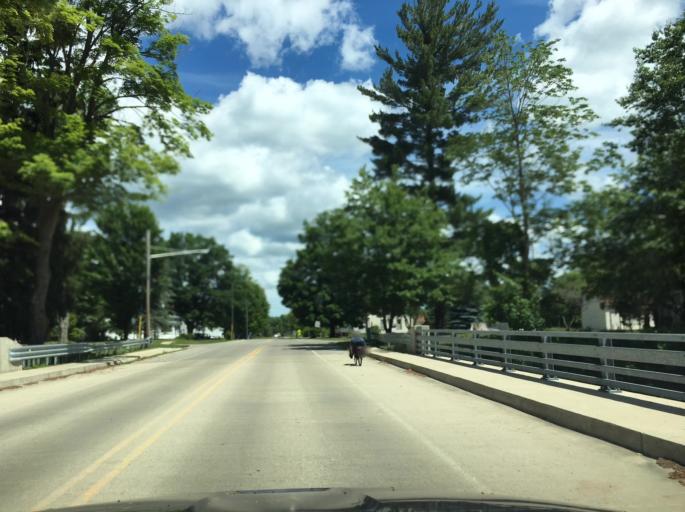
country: US
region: Michigan
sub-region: Osceola County
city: Reed City
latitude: 43.8528
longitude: -85.4444
